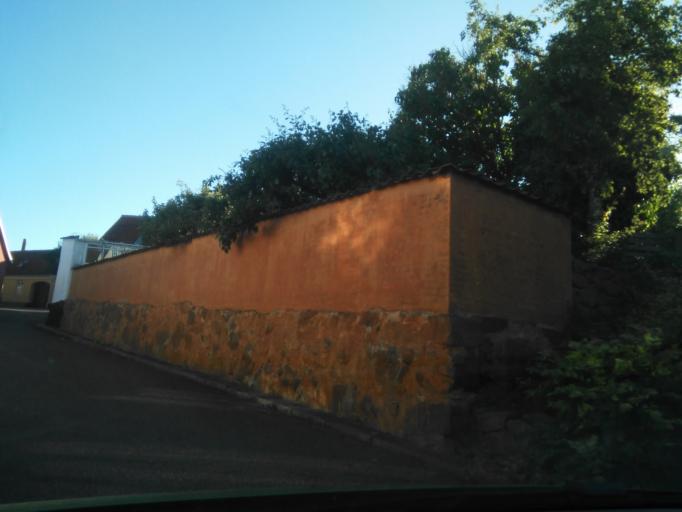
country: DK
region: Capital Region
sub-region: Bornholm Kommune
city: Ronne
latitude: 55.2752
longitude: 14.8035
